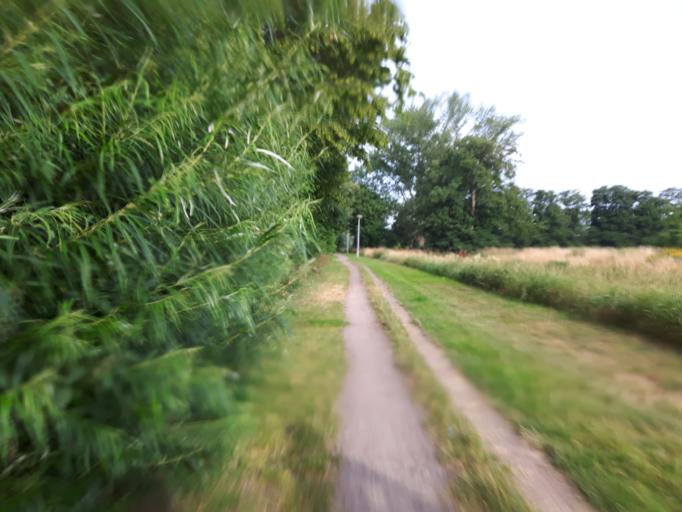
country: DE
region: Lower Saxony
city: Delmenhorst
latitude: 53.0631
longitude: 8.6602
